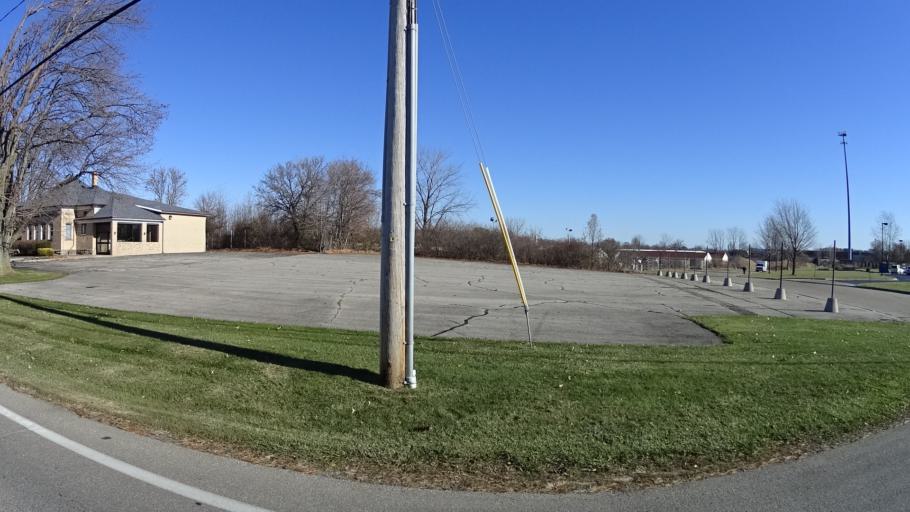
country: US
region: Ohio
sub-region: Lorain County
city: Elyria
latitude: 41.3730
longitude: -82.1486
